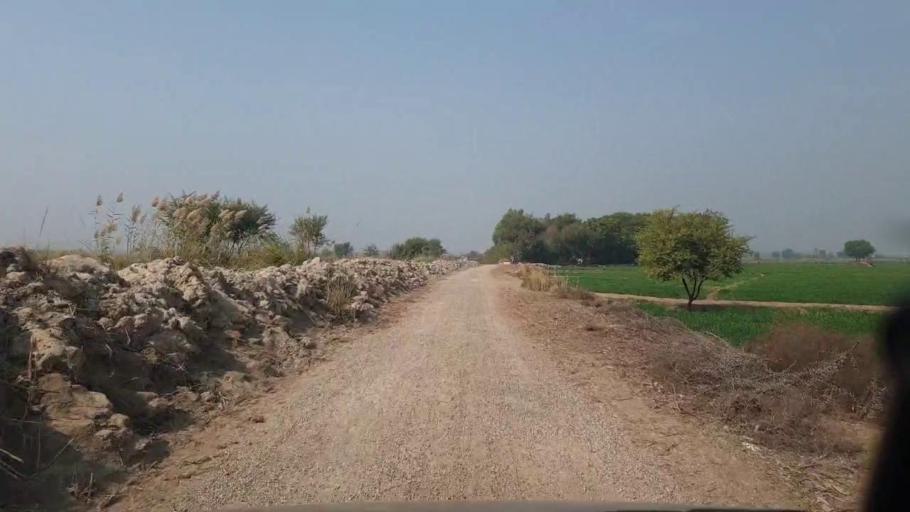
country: PK
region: Sindh
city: Shahdadpur
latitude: 26.0295
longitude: 68.5290
